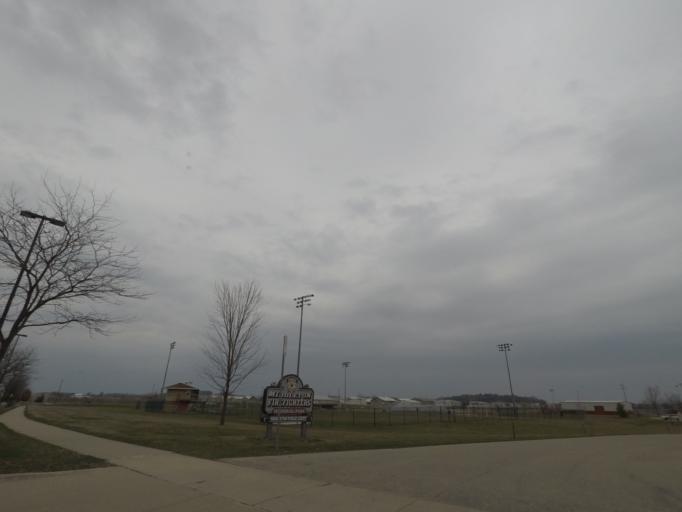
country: US
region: Wisconsin
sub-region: Dane County
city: Middleton
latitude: 43.1095
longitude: -89.5377
